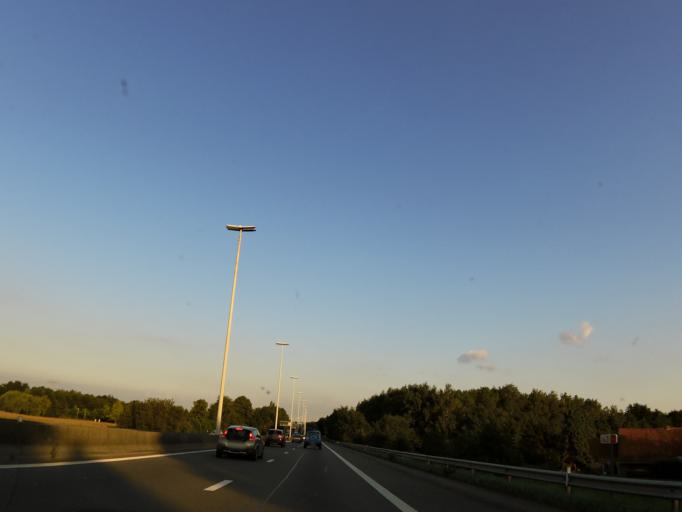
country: BE
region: Flanders
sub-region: Provincie Antwerpen
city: Nijlen
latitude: 51.1855
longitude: 4.6710
